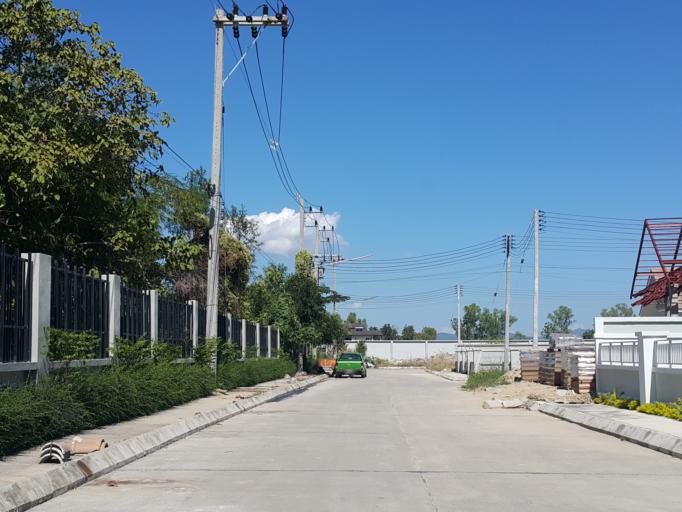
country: TH
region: Chiang Mai
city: San Sai
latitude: 18.8123
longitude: 99.0637
